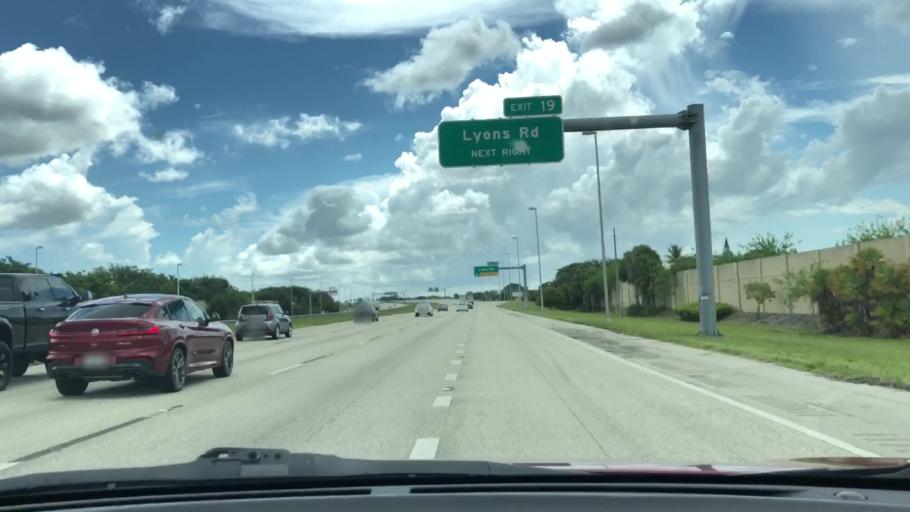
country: US
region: Florida
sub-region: Broward County
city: Parkland
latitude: 26.2998
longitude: -80.1955
